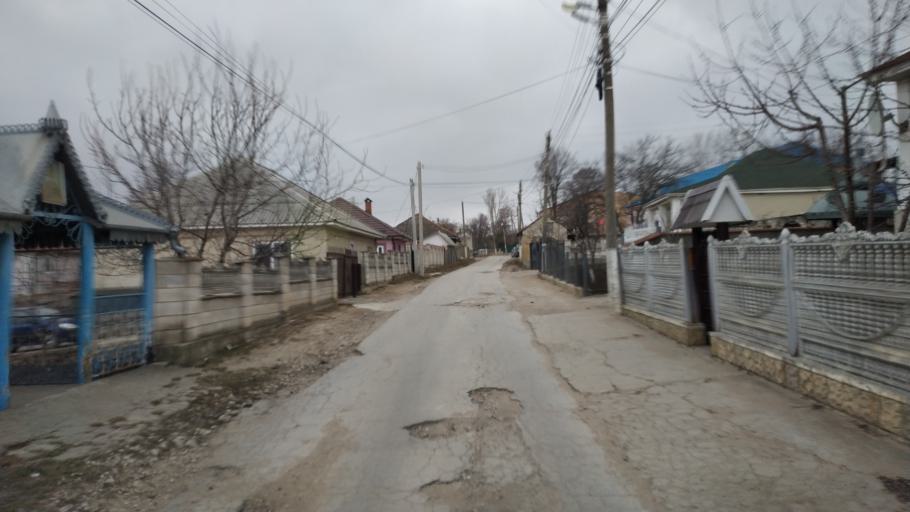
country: MD
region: Laloveni
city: Ialoveni
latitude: 46.9103
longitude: 28.8057
